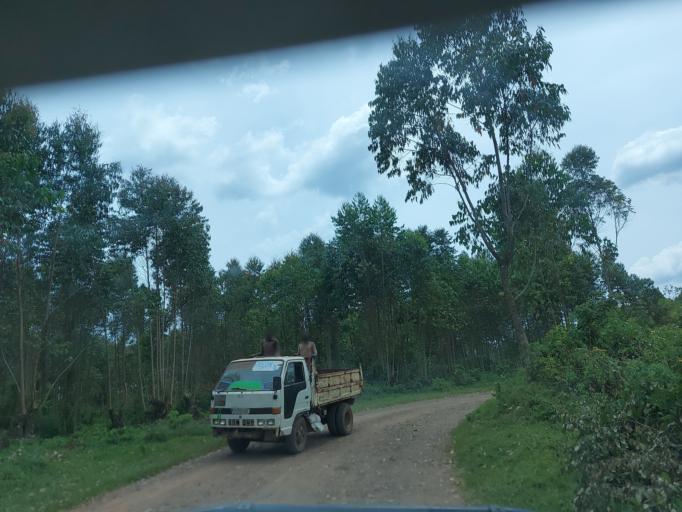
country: CD
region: South Kivu
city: Bukavu
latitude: -2.2449
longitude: 28.8239
